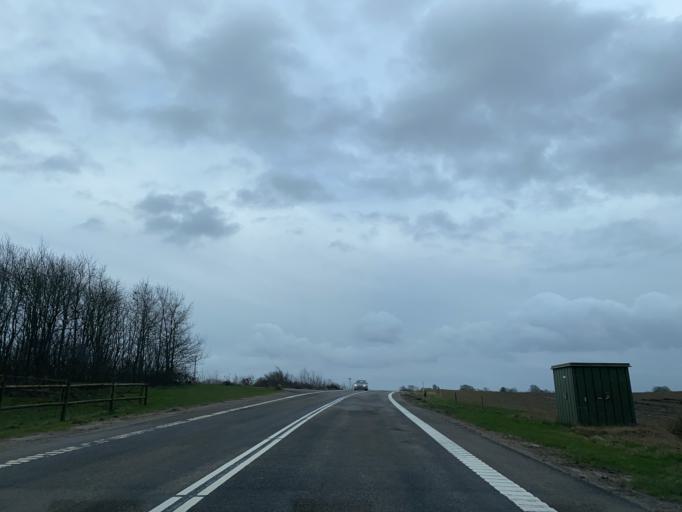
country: DK
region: Central Jutland
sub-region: Viborg Kommune
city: Bjerringbro
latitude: 56.2961
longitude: 9.6012
